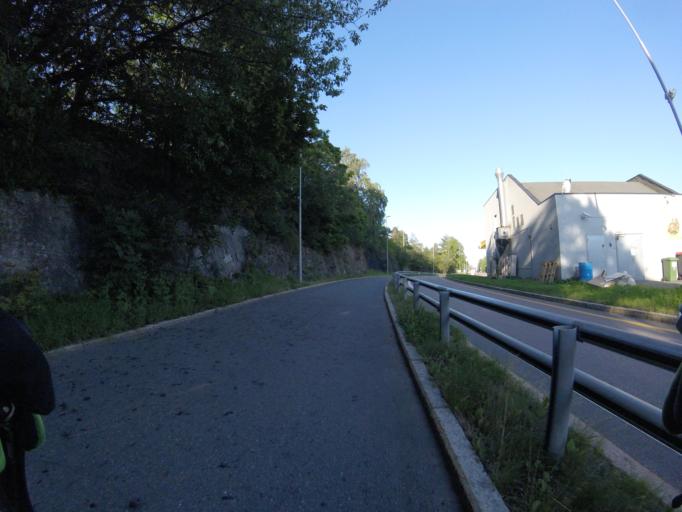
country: NO
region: Oslo
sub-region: Oslo
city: Oslo
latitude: 59.9442
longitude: 10.8326
